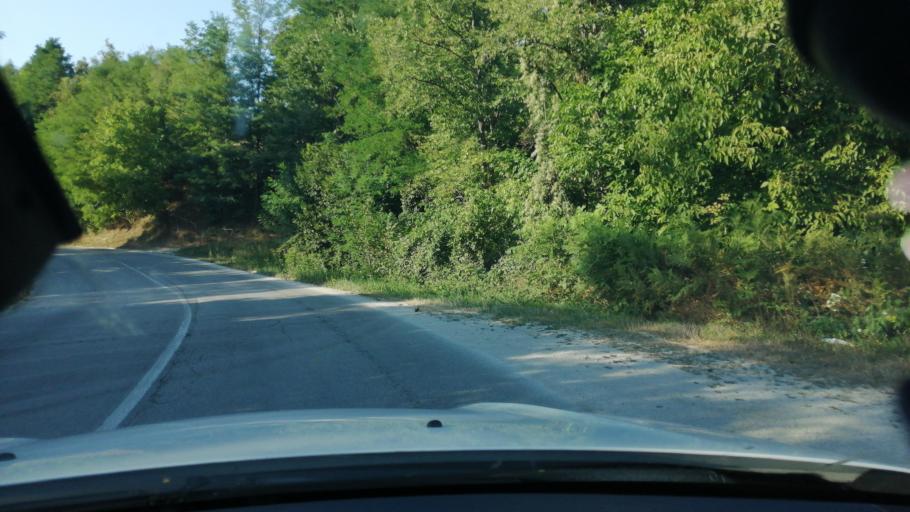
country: RS
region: Central Serbia
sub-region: Moravicki Okrug
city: Ivanjica
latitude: 43.7216
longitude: 20.2473
